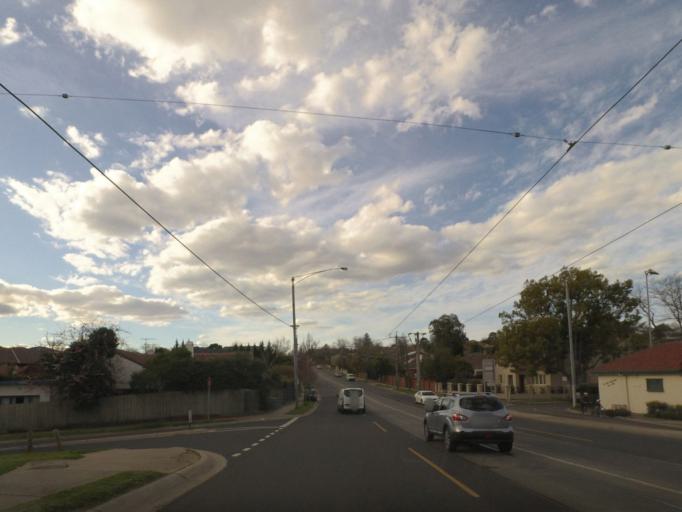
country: AU
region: Victoria
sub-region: Stonnington
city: Glen Iris
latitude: -37.8504
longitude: 145.0528
